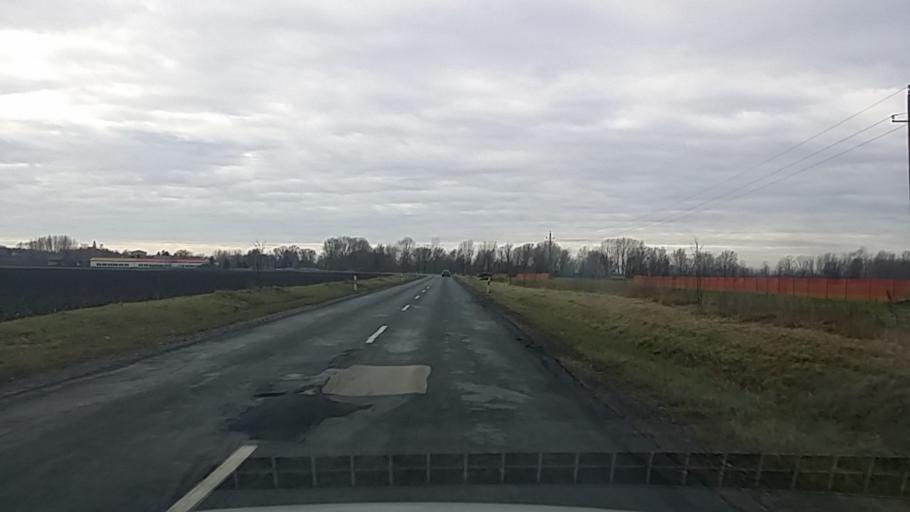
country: HU
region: Veszprem
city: Papa
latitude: 47.2956
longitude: 17.3771
